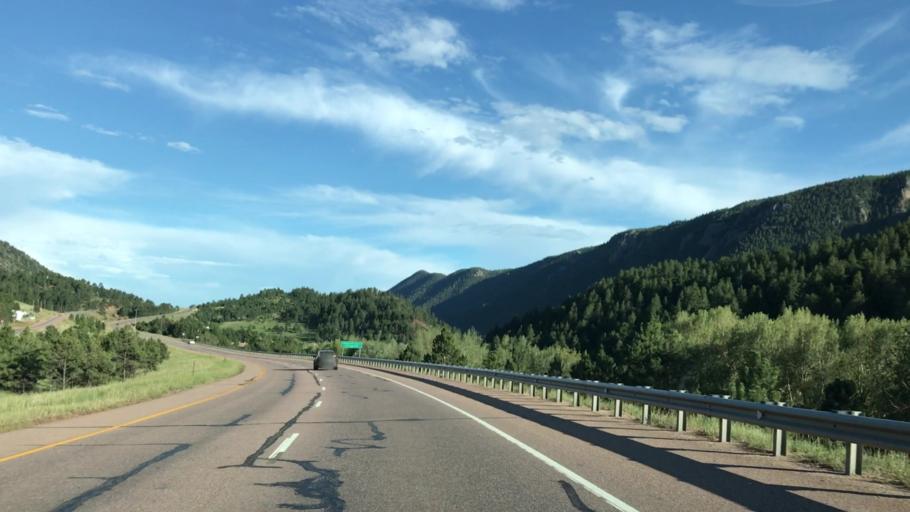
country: US
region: Colorado
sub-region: El Paso County
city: Cascade-Chipita Park
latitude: 38.9444
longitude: -105.0202
